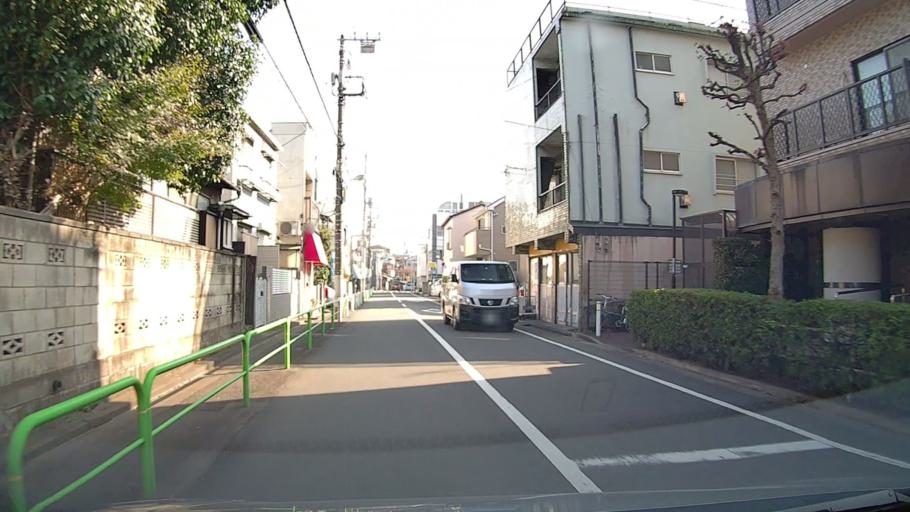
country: JP
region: Saitama
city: Kawaguchi
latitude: 35.7537
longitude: 139.6823
